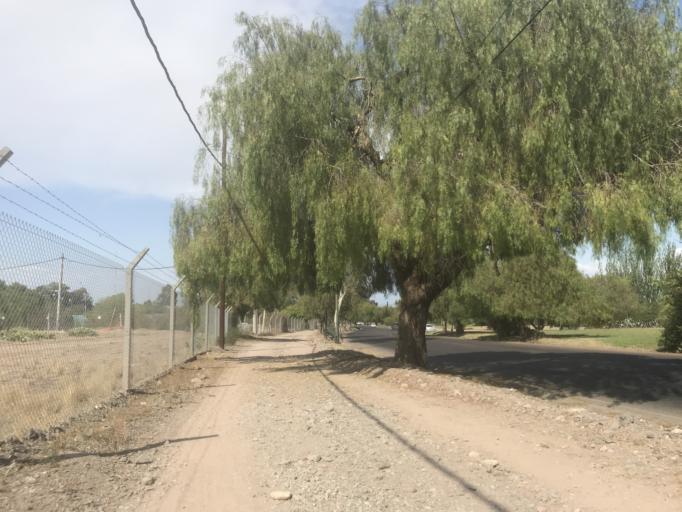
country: AR
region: Mendoza
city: Mendoza
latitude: -32.8828
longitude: -68.8872
